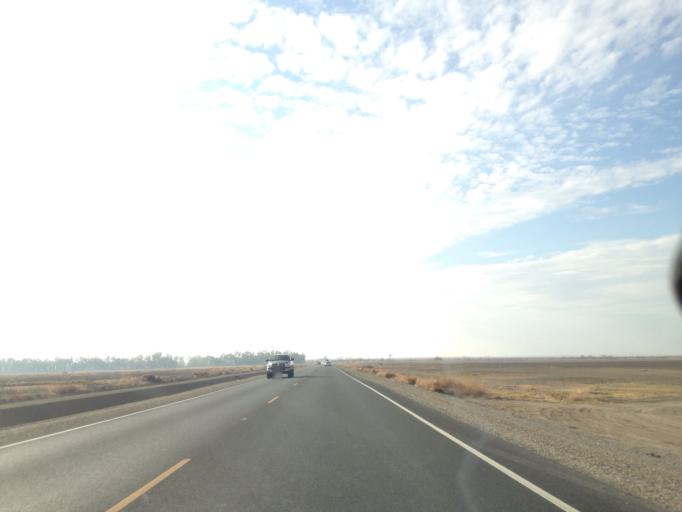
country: US
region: California
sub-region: Kern County
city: Lost Hills
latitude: 35.6162
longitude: -119.6344
